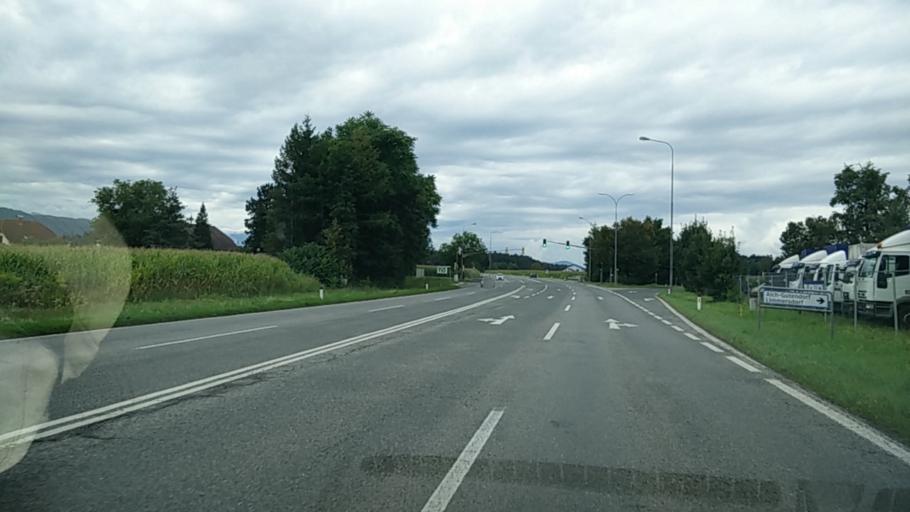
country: AT
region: Carinthia
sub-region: Politischer Bezirk Klagenfurt Land
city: Ebenthal
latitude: 46.6262
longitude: 14.3895
